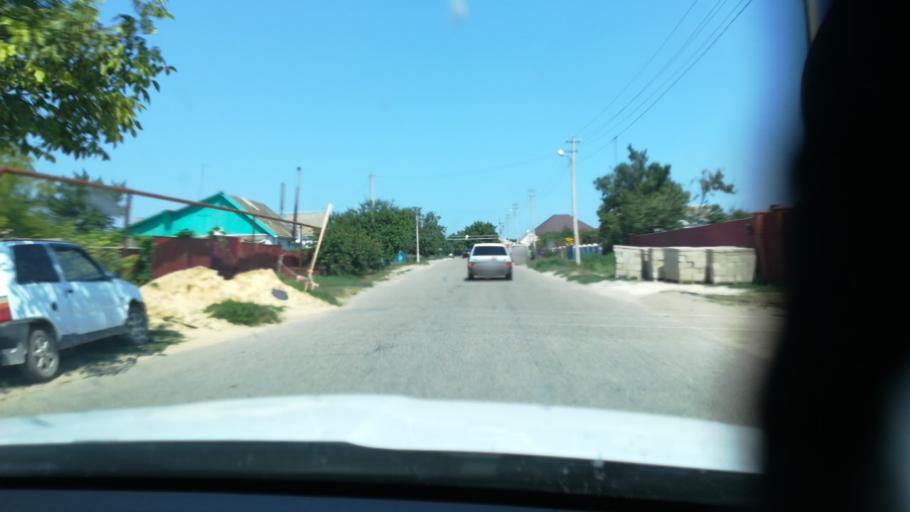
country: RU
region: Krasnodarskiy
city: Starotitarovskaya
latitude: 45.2122
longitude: 37.1444
